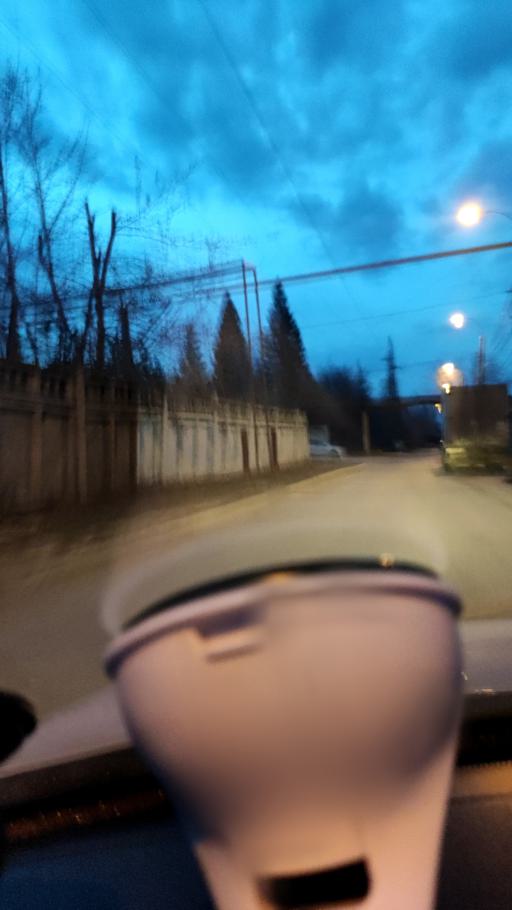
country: RU
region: Samara
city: Volzhskiy
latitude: 53.3510
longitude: 50.2087
